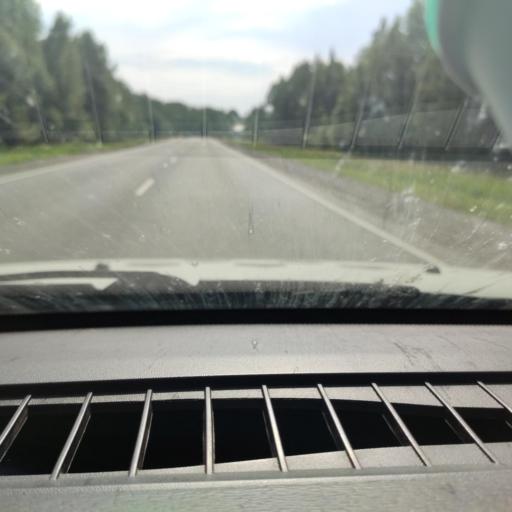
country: RU
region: Kirov
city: Kostino
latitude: 58.8574
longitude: 53.1028
